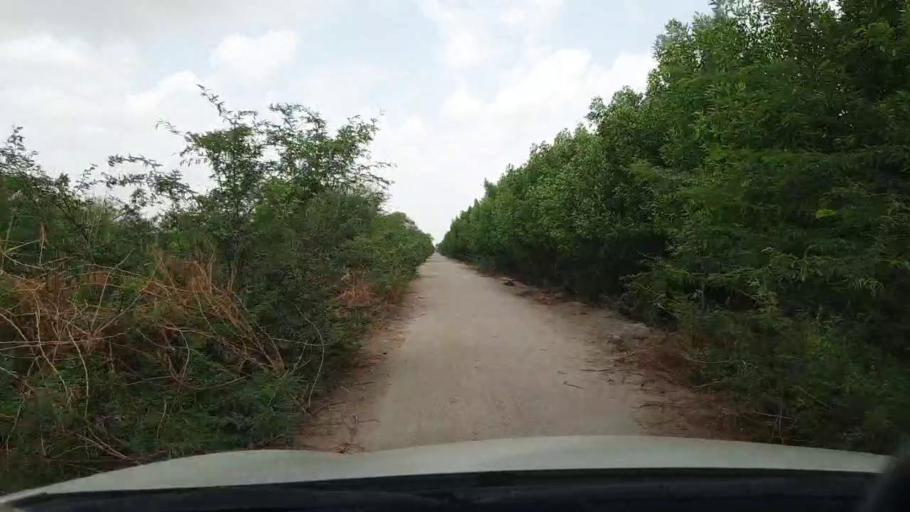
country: PK
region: Sindh
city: Kadhan
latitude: 24.3603
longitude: 68.9594
